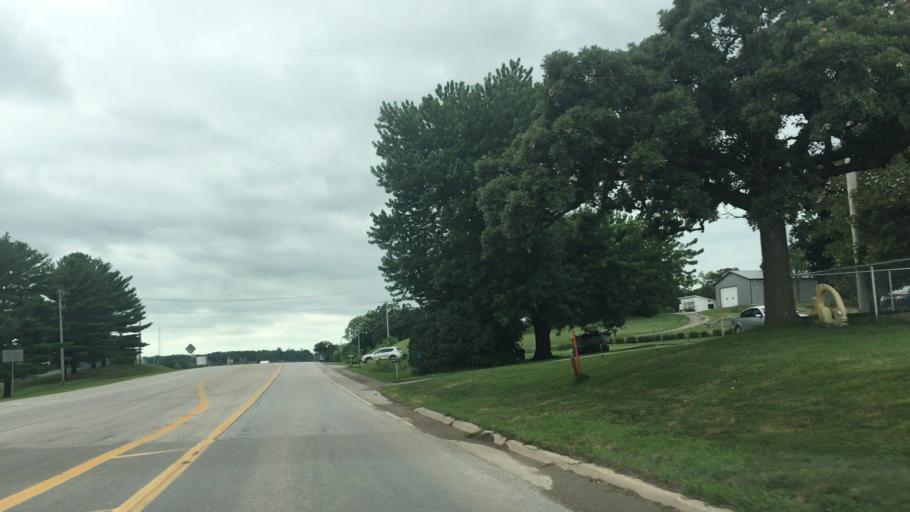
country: US
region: Iowa
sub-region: Johnson County
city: Tiffin
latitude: 41.7074
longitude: -91.6672
